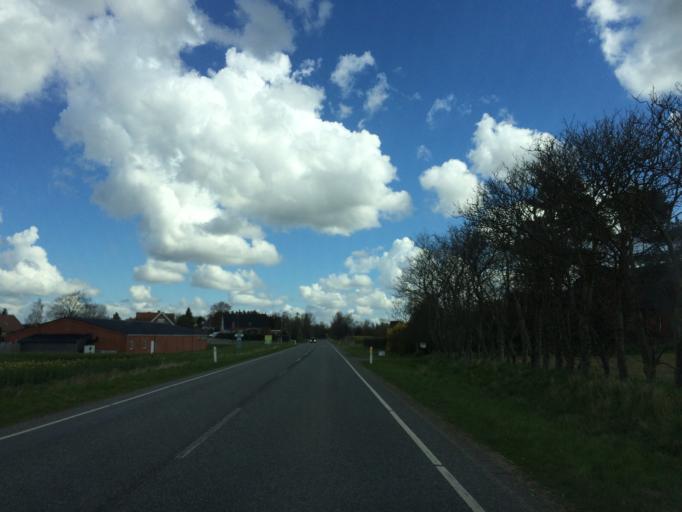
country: DK
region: South Denmark
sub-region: Assens Kommune
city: Tommerup
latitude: 55.2478
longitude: 10.2281
